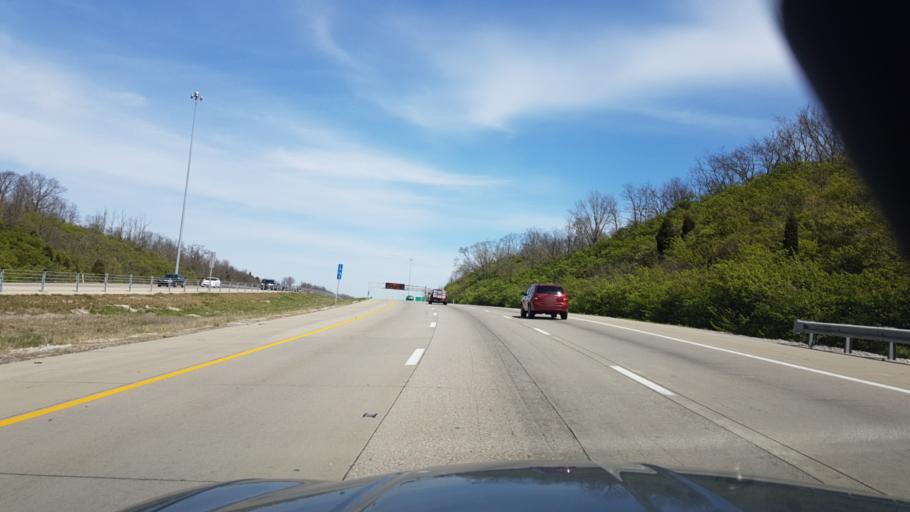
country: US
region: Kentucky
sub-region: Campbell County
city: Highland Heights
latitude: 39.0303
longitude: -84.4705
